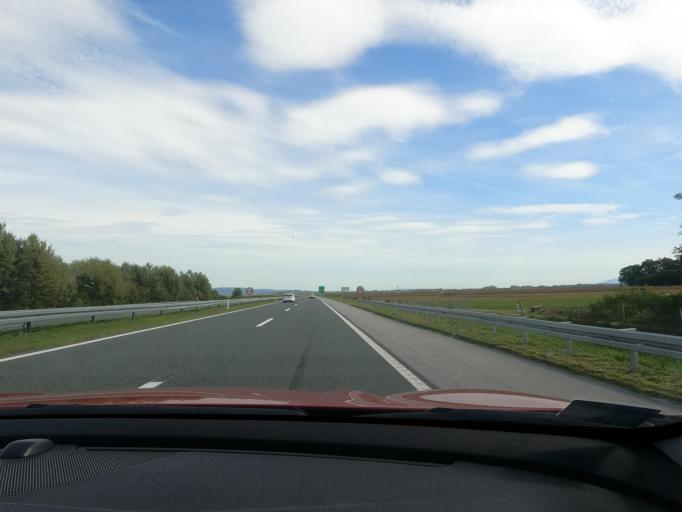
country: HR
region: Brodsko-Posavska
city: Ljupina
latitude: 45.2258
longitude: 17.3902
